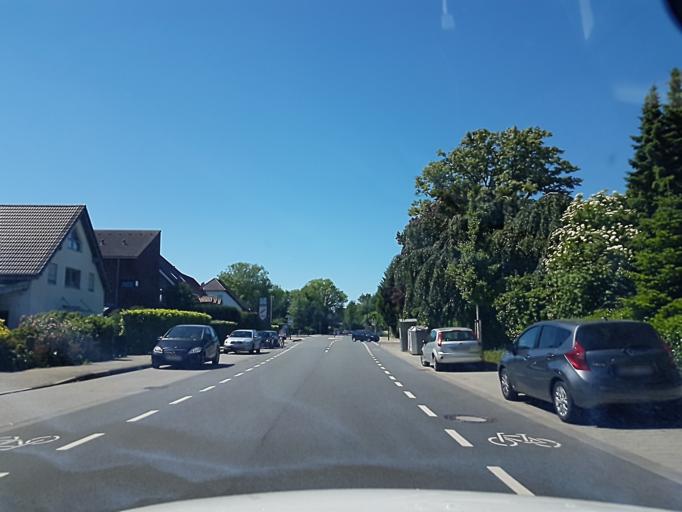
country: DE
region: North Rhine-Westphalia
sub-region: Regierungsbezirk Dusseldorf
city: Ratingen
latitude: 51.3267
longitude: 6.7767
